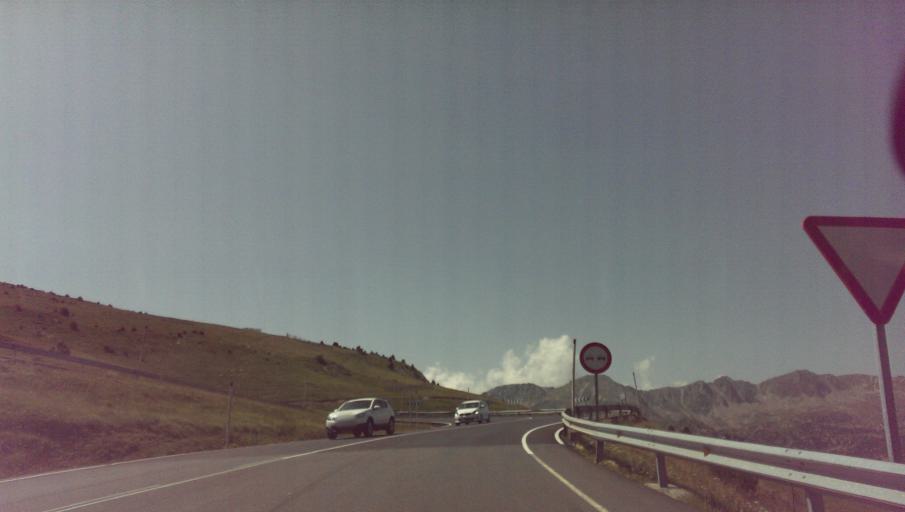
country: AD
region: Encamp
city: Pas de la Casa
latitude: 42.5407
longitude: 1.7137
